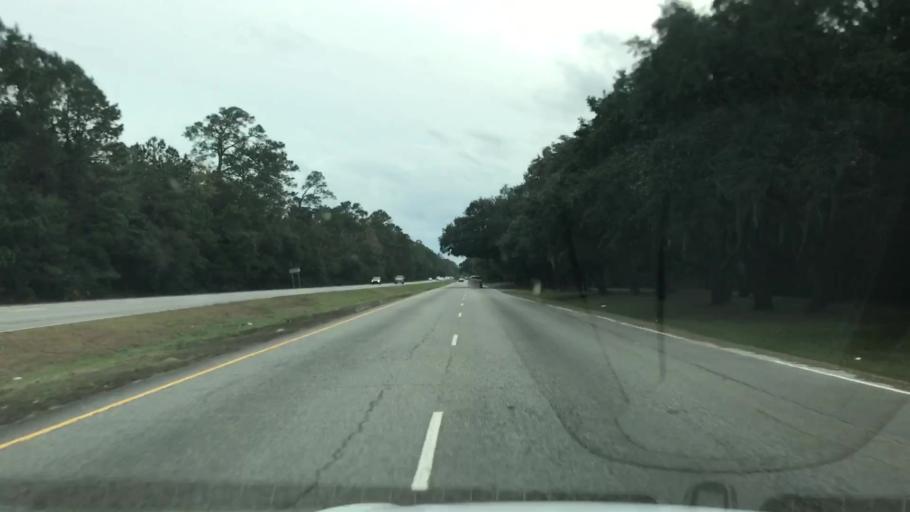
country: US
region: South Carolina
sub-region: Georgetown County
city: Murrells Inlet
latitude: 33.5076
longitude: -79.0779
